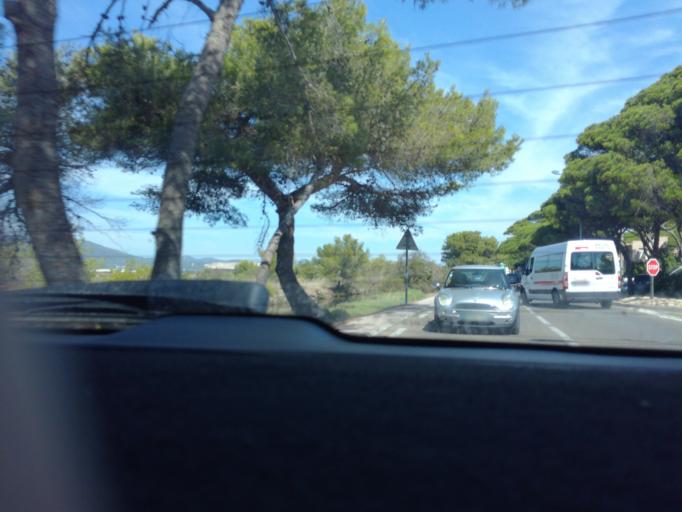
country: FR
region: Provence-Alpes-Cote d'Azur
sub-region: Departement du Var
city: Hyeres
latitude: 43.0623
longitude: 6.1472
